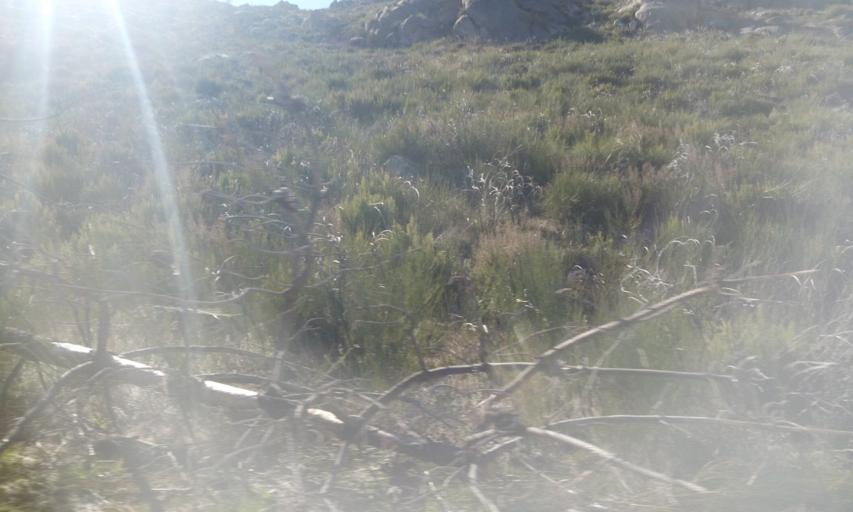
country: PT
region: Guarda
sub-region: Manteigas
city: Manteigas
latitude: 40.4850
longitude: -7.5176
